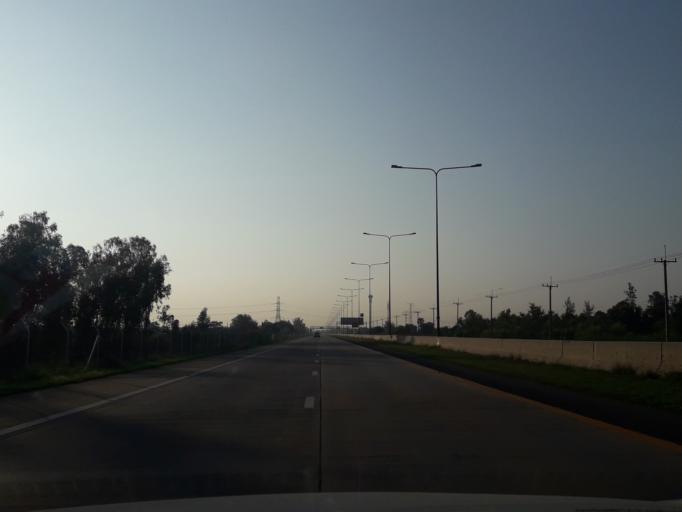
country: TH
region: Pathum Thani
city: Sam Khok
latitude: 14.1398
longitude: 100.5611
